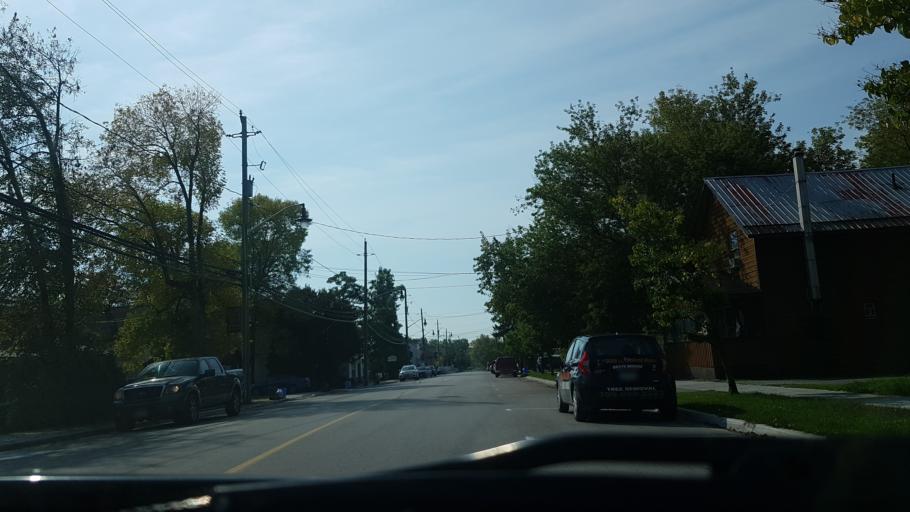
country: CA
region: Ontario
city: Gravenhurst
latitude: 44.7521
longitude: -79.3331
